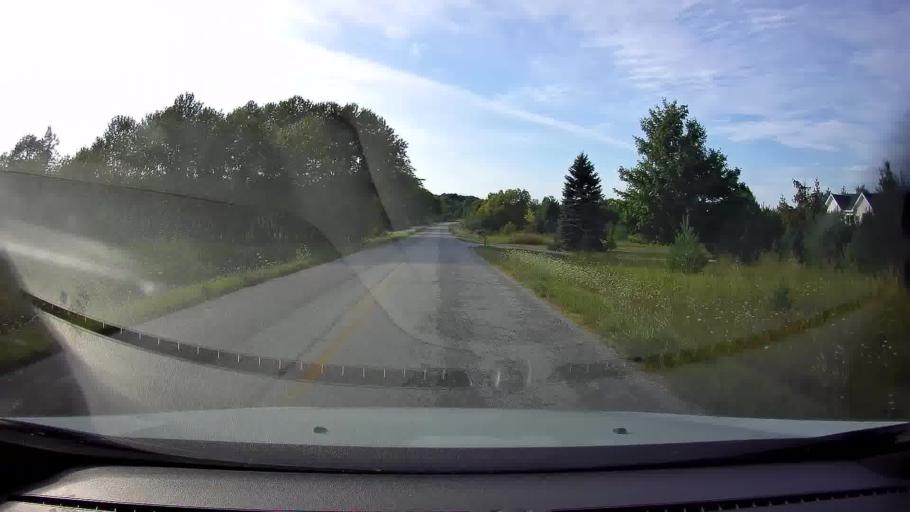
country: US
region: Wisconsin
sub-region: Door County
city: Sturgeon Bay
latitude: 45.1751
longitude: -87.1399
